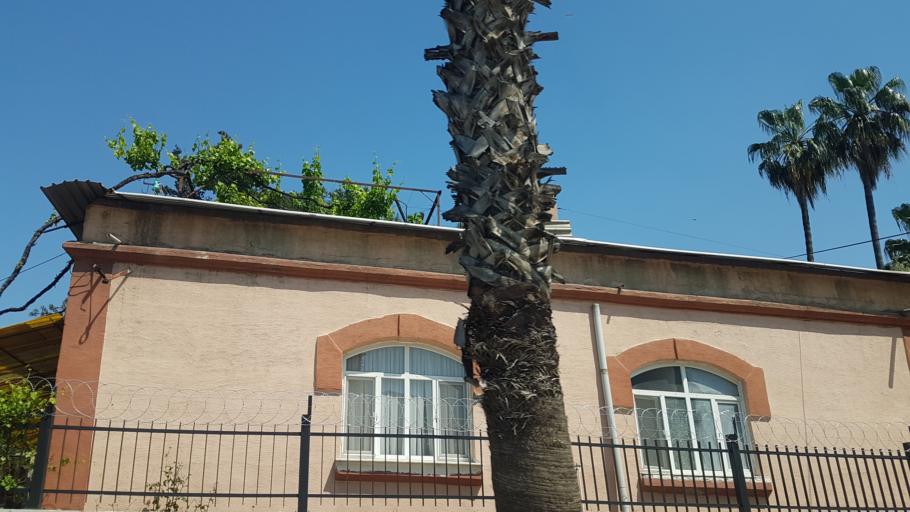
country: TR
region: Adana
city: Adana
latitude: 37.0123
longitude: 35.3372
